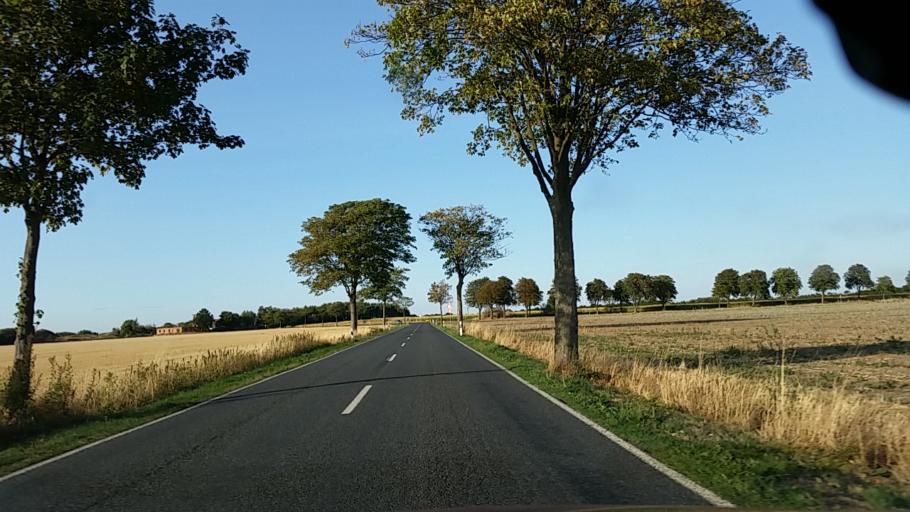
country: DE
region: Lower Saxony
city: Calberlah
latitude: 52.3811
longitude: 10.6435
